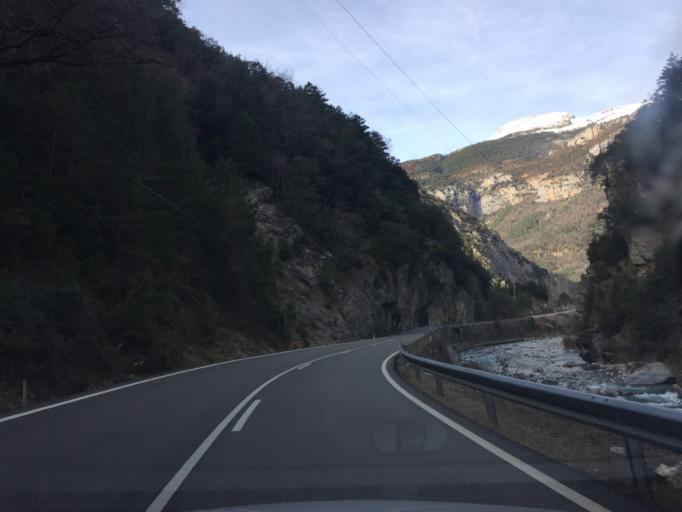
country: ES
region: Aragon
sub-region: Provincia de Huesca
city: Bielsa
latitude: 42.5696
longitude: 0.2050
